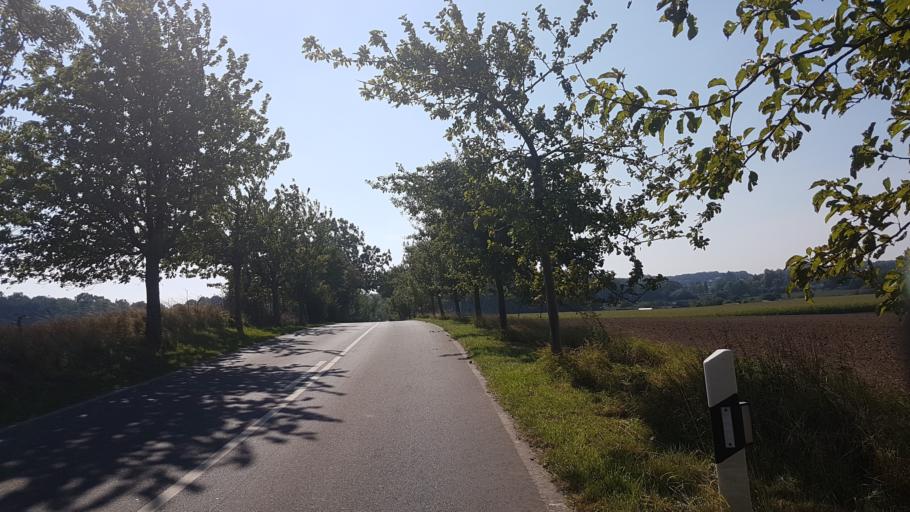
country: DE
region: Mecklenburg-Vorpommern
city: Putbus
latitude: 54.3503
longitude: 13.5082
